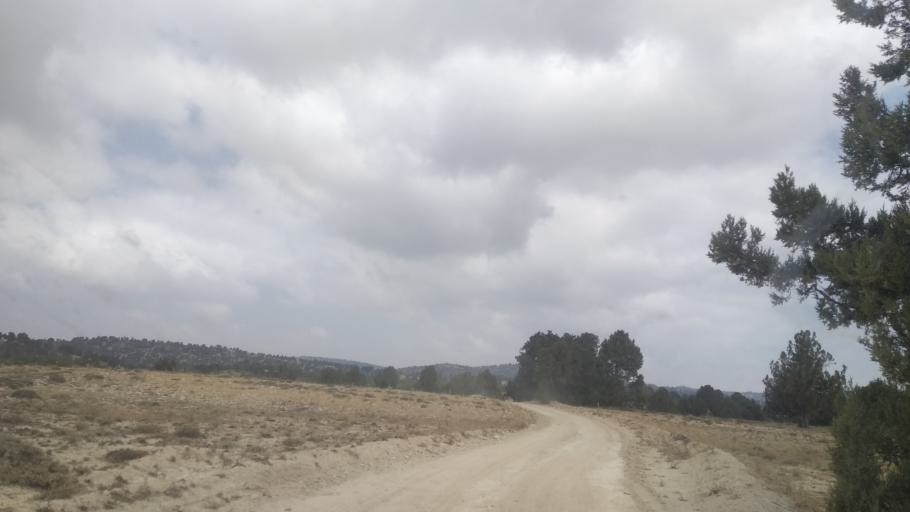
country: TR
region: Mersin
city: Sarikavak
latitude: 36.5747
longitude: 33.7570
